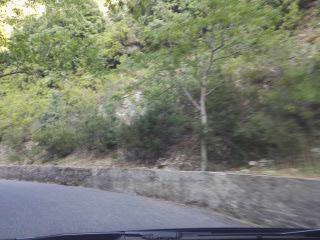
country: IT
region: Calabria
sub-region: Provincia di Vibo-Valentia
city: Nardodipace
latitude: 38.4333
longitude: 16.3426
